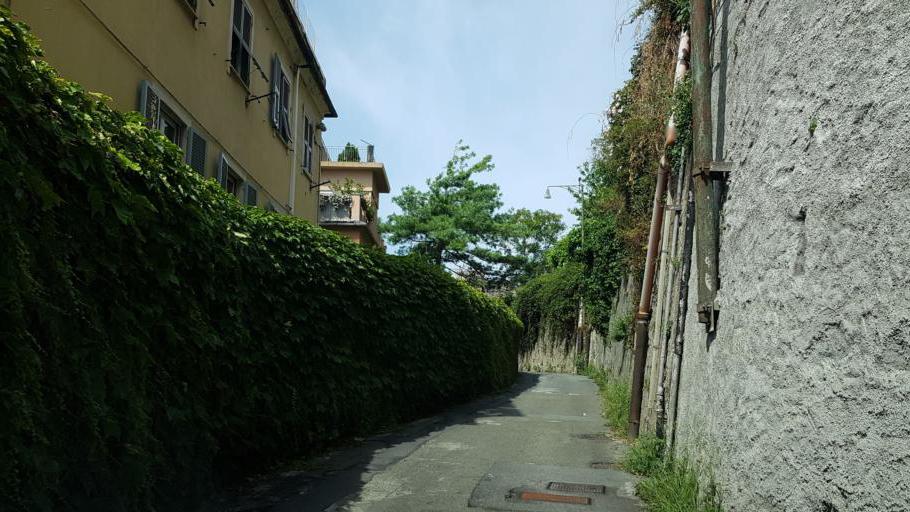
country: IT
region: Liguria
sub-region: Provincia di Genova
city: San Teodoro
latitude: 44.4162
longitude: 8.8649
